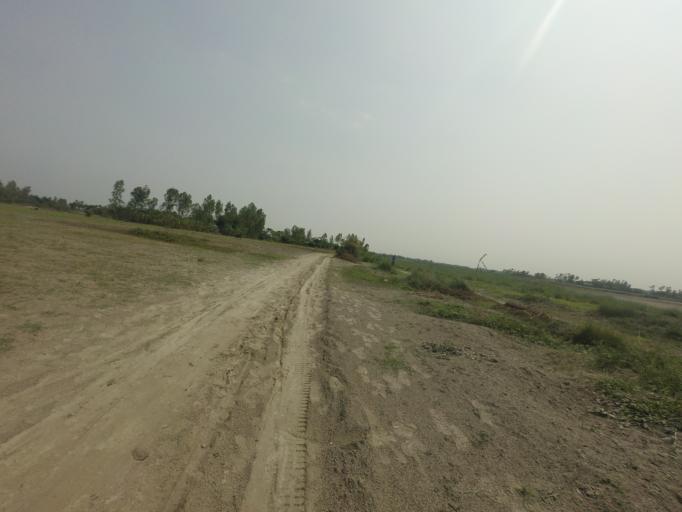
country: BD
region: Rajshahi
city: Sirajganj
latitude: 24.3546
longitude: 89.7269
